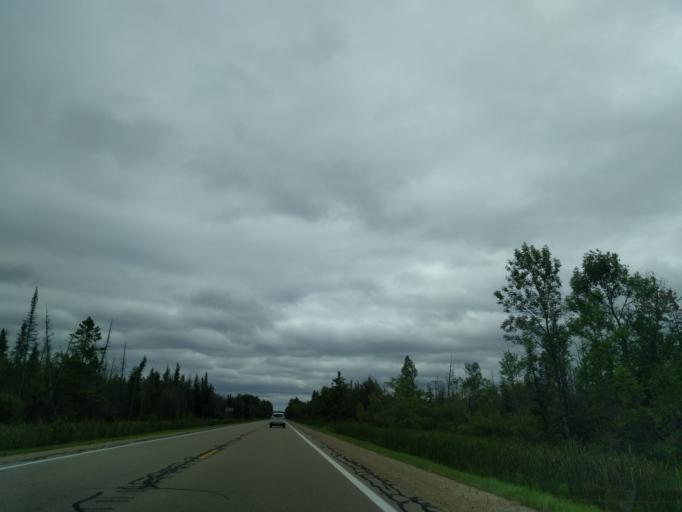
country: US
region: Michigan
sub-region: Menominee County
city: Menominee
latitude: 45.3942
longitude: -87.3683
